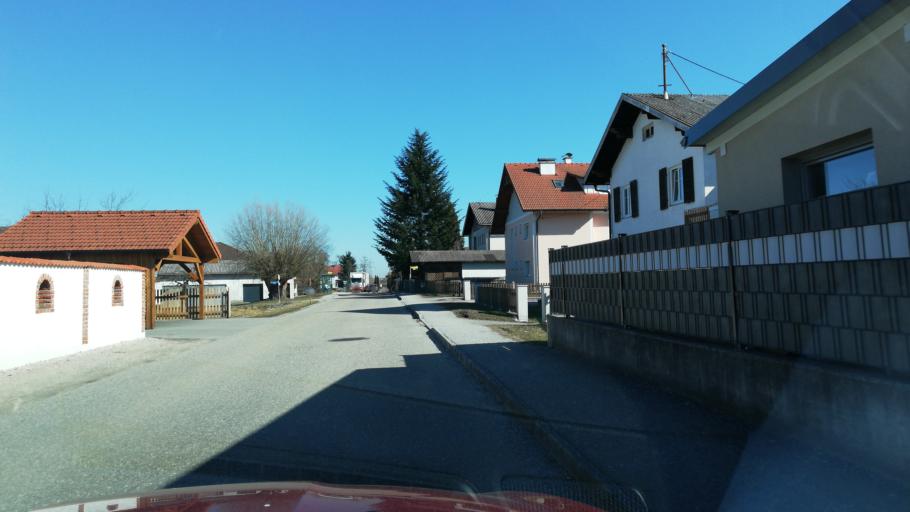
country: AT
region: Upper Austria
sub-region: Politischer Bezirk Vocklabruck
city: Redlham
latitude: 48.0274
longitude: 13.7312
